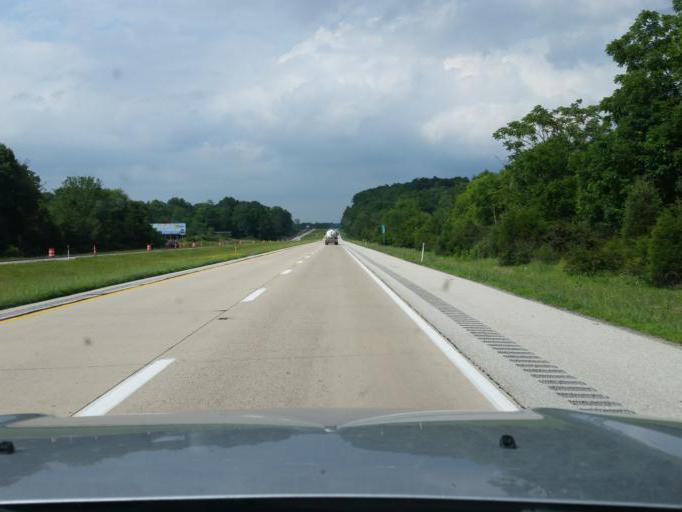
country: US
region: Maryland
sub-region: Frederick County
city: Emmitsburg
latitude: 39.7529
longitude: -77.2696
